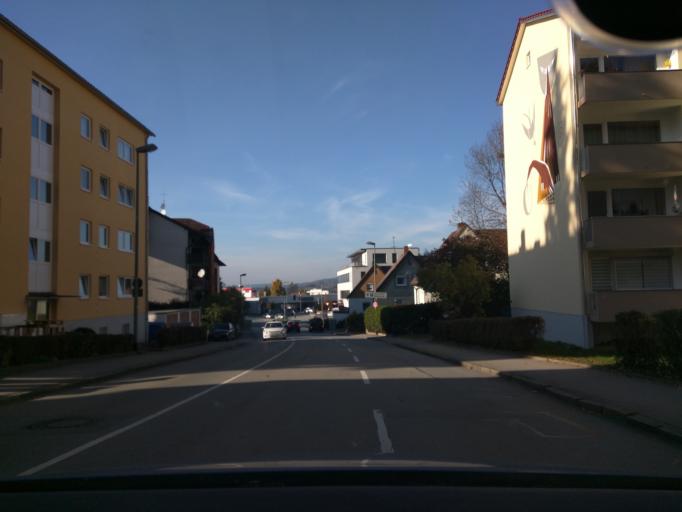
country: DE
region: Bavaria
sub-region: Lower Bavaria
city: Passau
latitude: 48.5691
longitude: 13.4231
